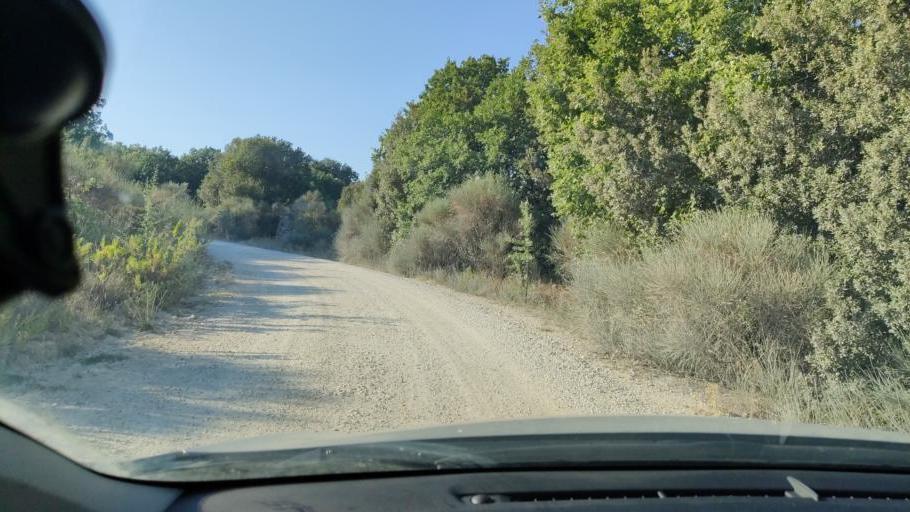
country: IT
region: Umbria
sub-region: Provincia di Terni
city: Amelia
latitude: 42.5380
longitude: 12.3793
